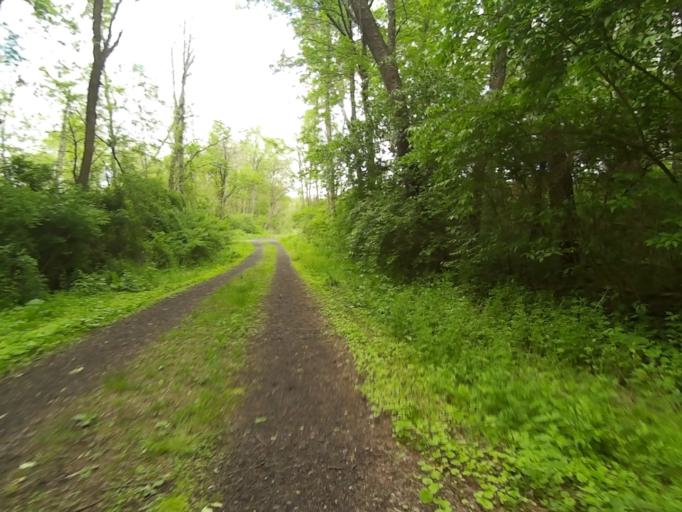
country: US
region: Pennsylvania
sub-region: Centre County
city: Park Forest Village
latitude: 40.8307
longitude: -77.8929
